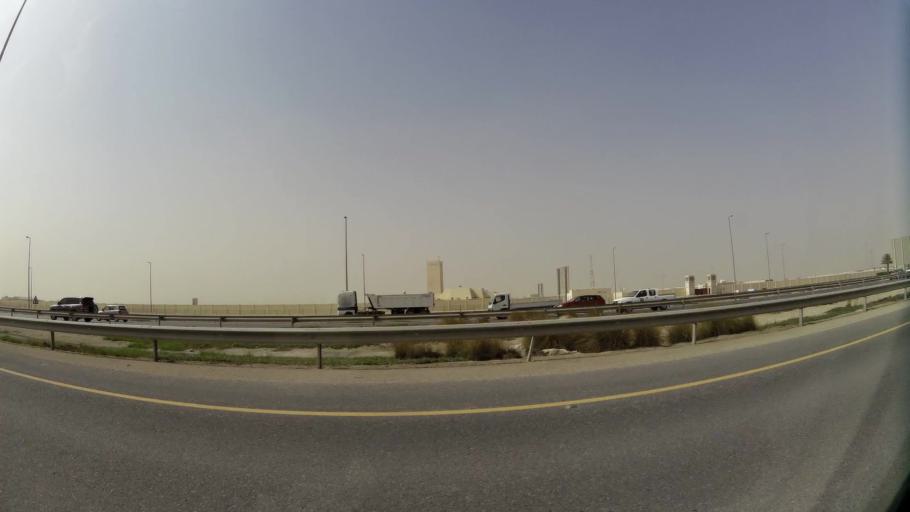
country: QA
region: Baladiyat ar Rayyan
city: Ar Rayyan
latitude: 25.2189
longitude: 51.4207
